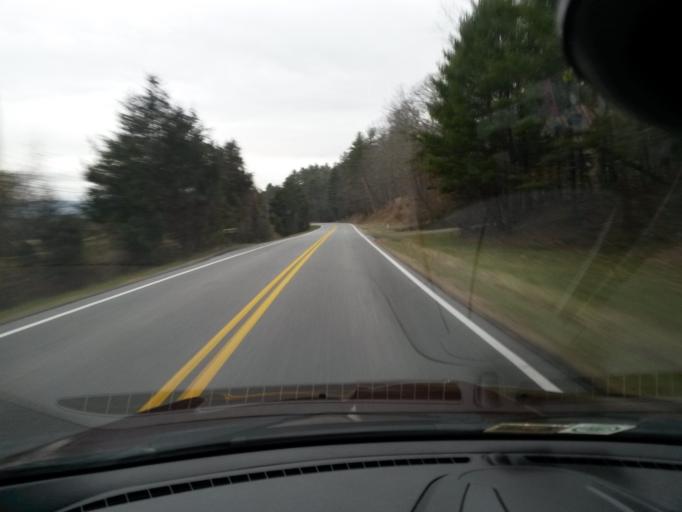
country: US
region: Virginia
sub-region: Bath County
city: Warm Springs
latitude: 38.0284
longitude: -79.6499
